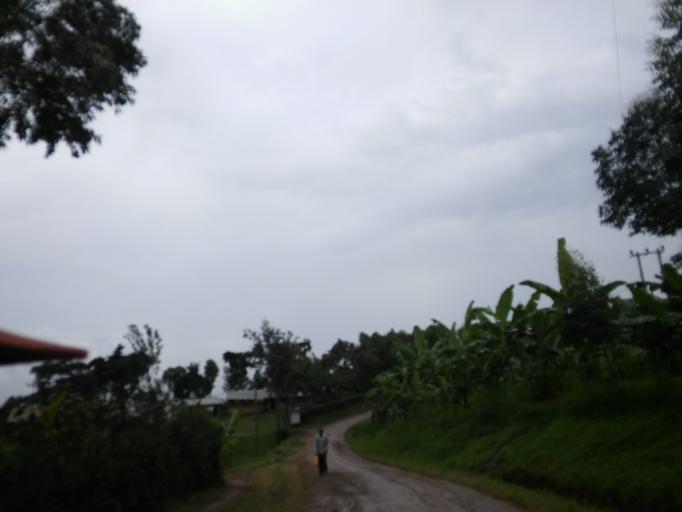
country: UG
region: Eastern Region
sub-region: Bududa District
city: Bududa
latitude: 1.0026
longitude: 34.2479
